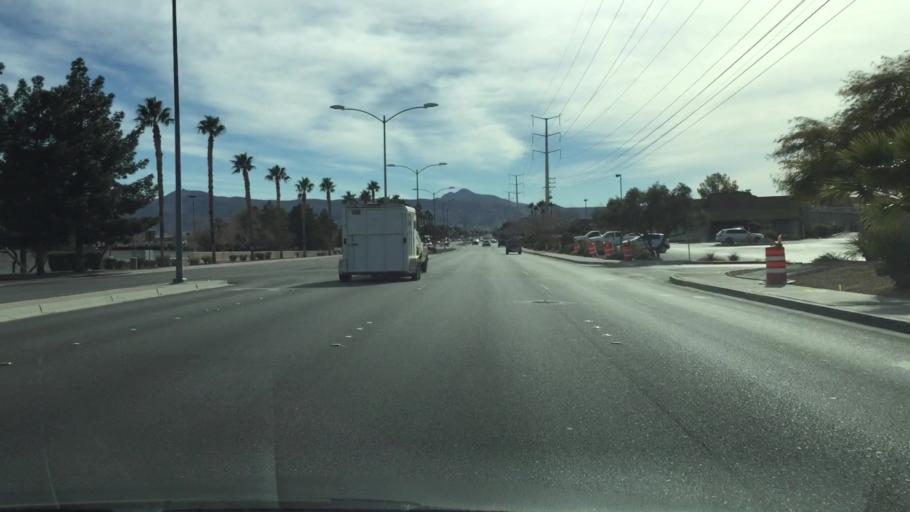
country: US
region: Nevada
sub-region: Clark County
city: Whitney
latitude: 36.0694
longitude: -115.0462
